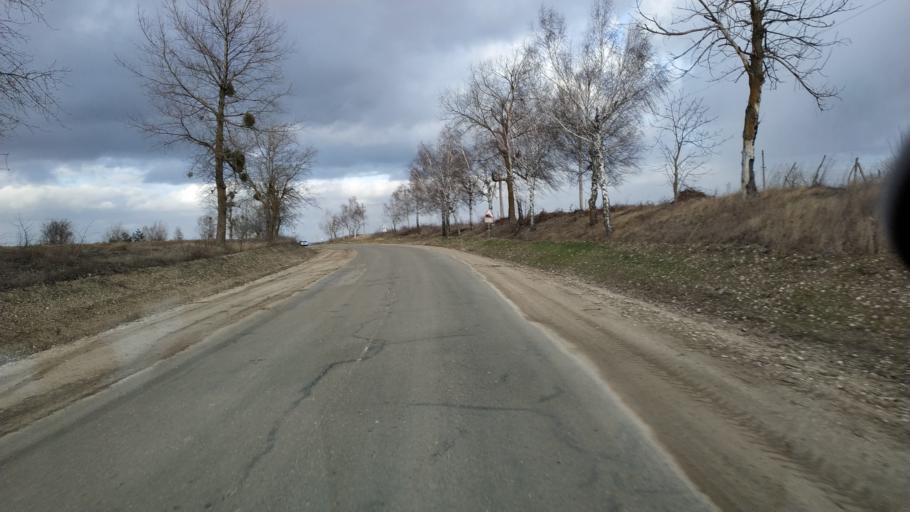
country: MD
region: Calarasi
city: Calarasi
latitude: 47.2878
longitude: 28.3570
